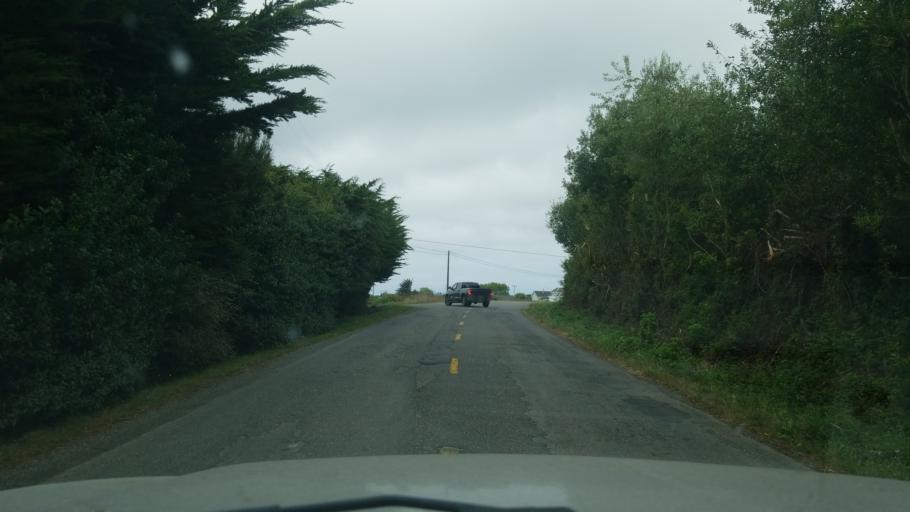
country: US
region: California
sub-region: Humboldt County
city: Ferndale
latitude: 40.5941
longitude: -124.2736
